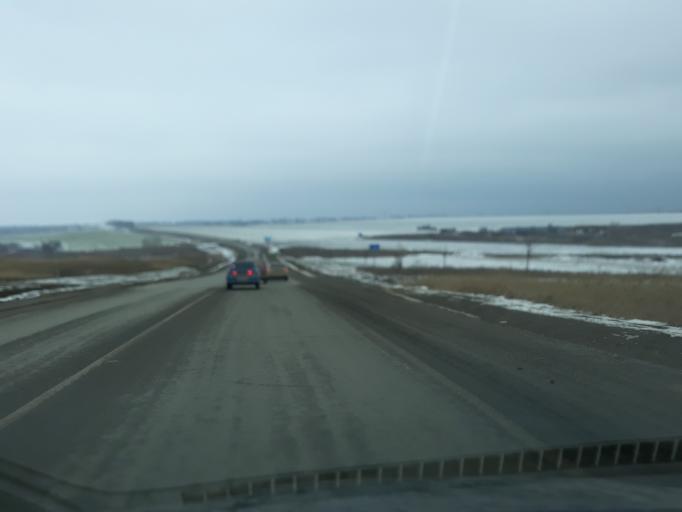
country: RU
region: Rostov
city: Primorka
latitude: 47.3121
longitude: 39.1100
